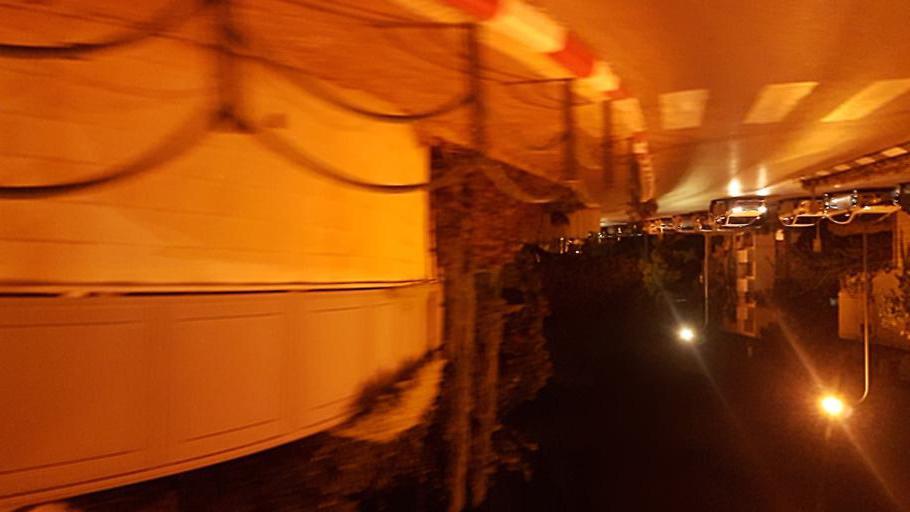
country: IL
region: Central District
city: Hod HaSharon
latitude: 32.1628
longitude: 34.8899
